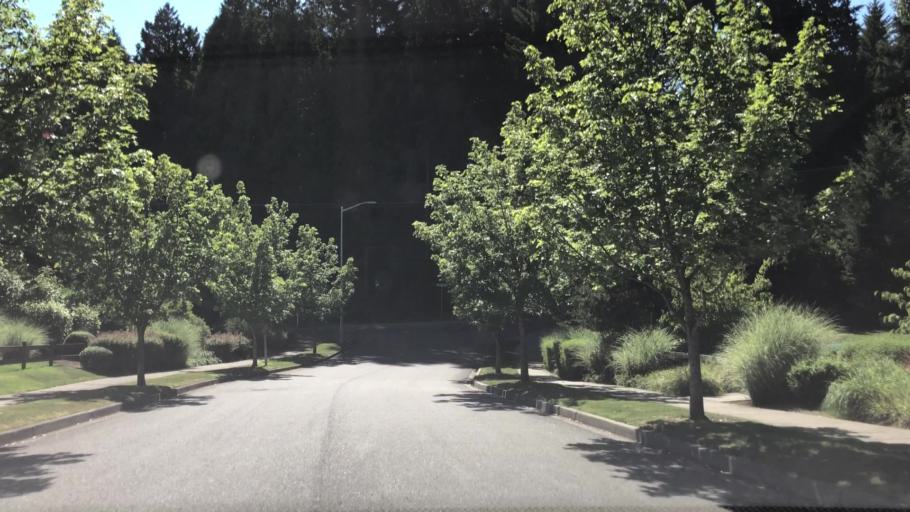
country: US
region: Washington
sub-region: Snohomish County
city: North Creek
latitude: 47.7891
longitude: -122.1855
